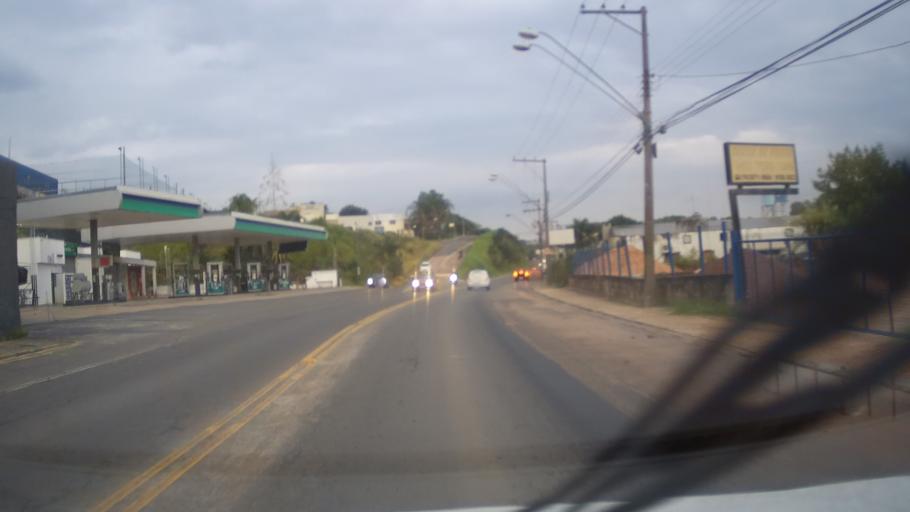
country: BR
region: Sao Paulo
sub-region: Valinhos
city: Valinhos
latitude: -22.9496
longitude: -46.9842
